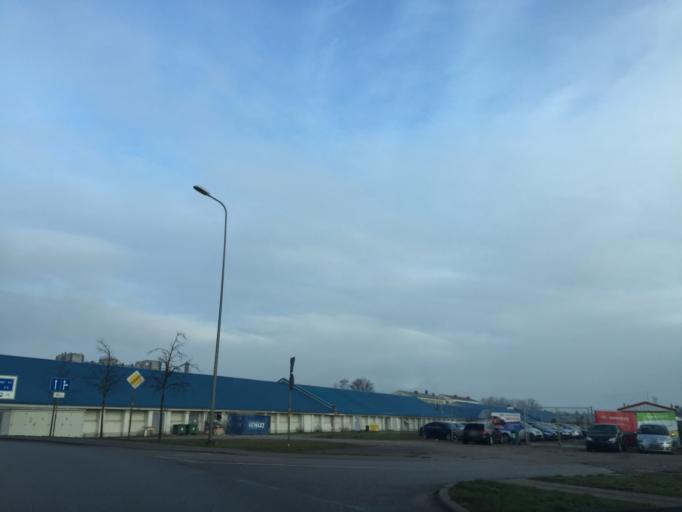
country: LV
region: Liepaja
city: Liepaja
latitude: 56.5212
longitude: 21.0280
